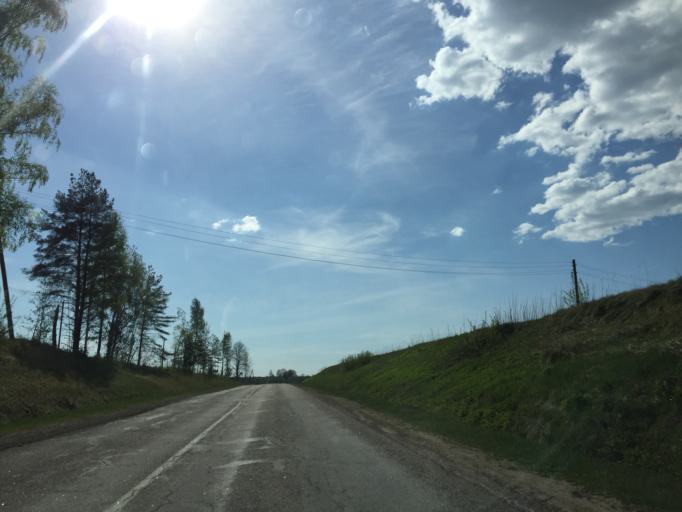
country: LV
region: Limbazu Rajons
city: Limbazi
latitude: 57.5128
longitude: 24.8052
